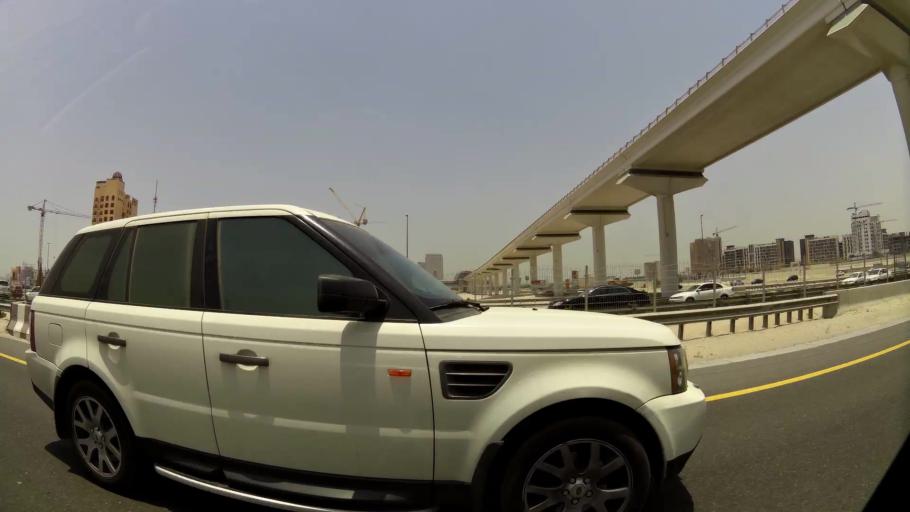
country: AE
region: Ash Shariqah
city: Sharjah
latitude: 25.2208
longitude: 55.3375
